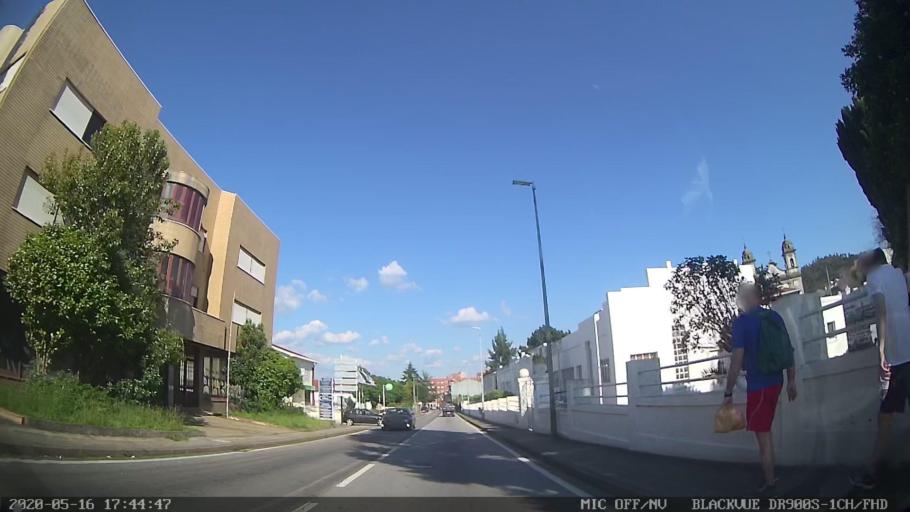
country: PT
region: Porto
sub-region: Valongo
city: Valongo
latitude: 41.1894
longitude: -8.5026
